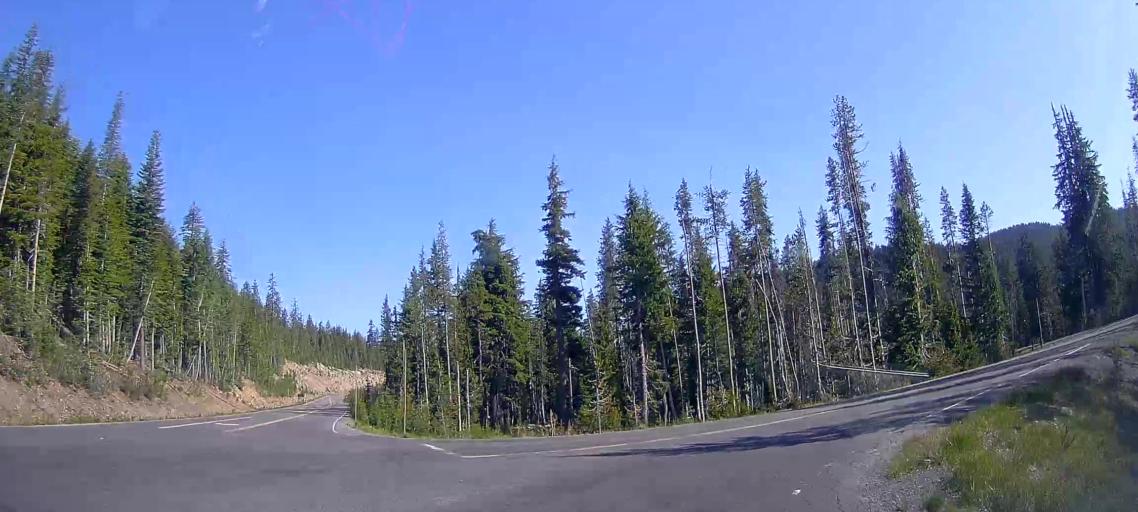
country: US
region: Oregon
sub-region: Jackson County
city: Shady Cove
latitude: 42.8656
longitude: -122.1687
